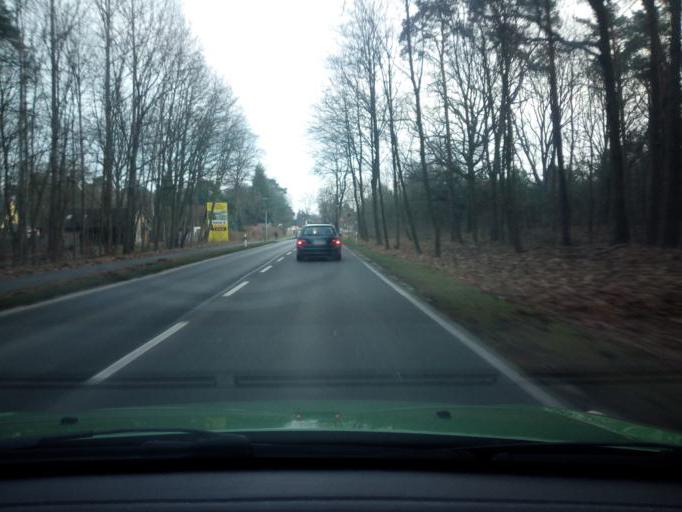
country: DE
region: Berlin
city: Muggelheim
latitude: 52.4176
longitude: 13.6528
